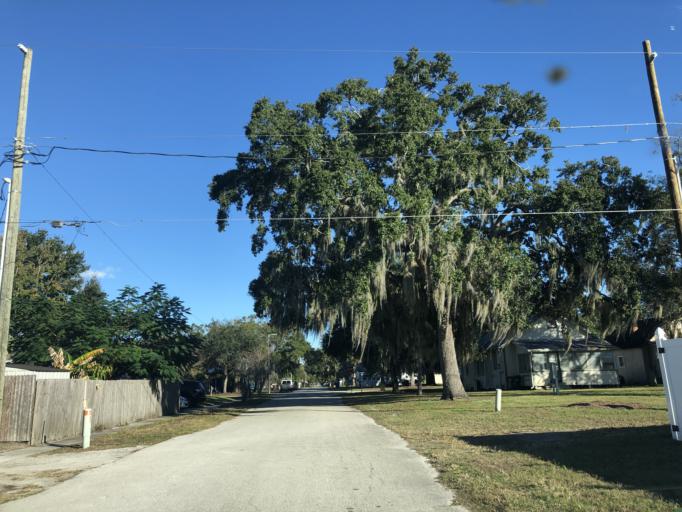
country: US
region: Florida
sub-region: Osceola County
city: Saint Cloud
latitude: 28.2506
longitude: -81.2822
